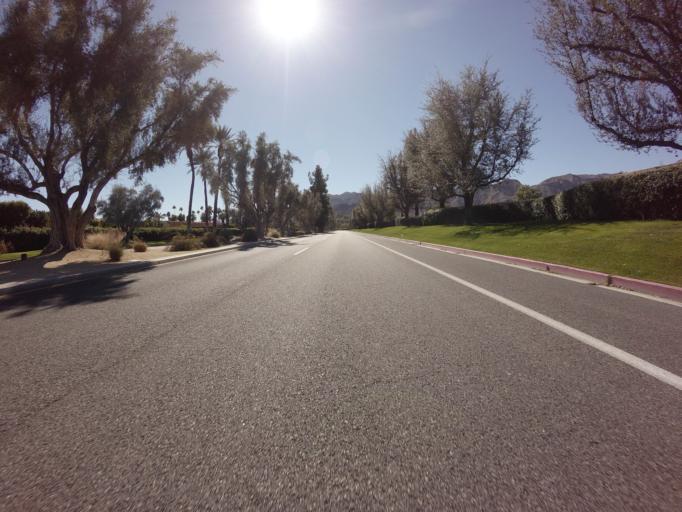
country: US
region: California
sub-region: Riverside County
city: Rancho Mirage
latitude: 33.7610
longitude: -116.4257
